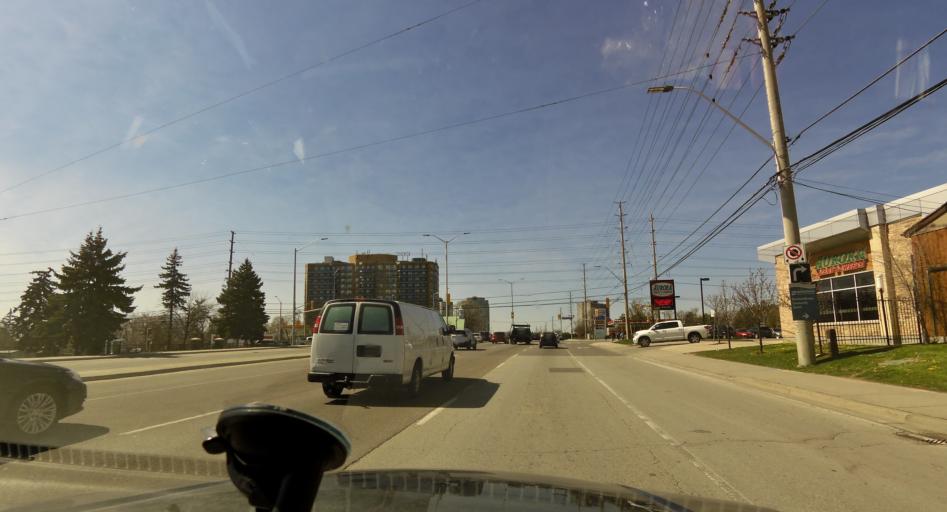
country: CA
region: Ontario
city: Etobicoke
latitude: 43.6219
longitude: -79.6016
